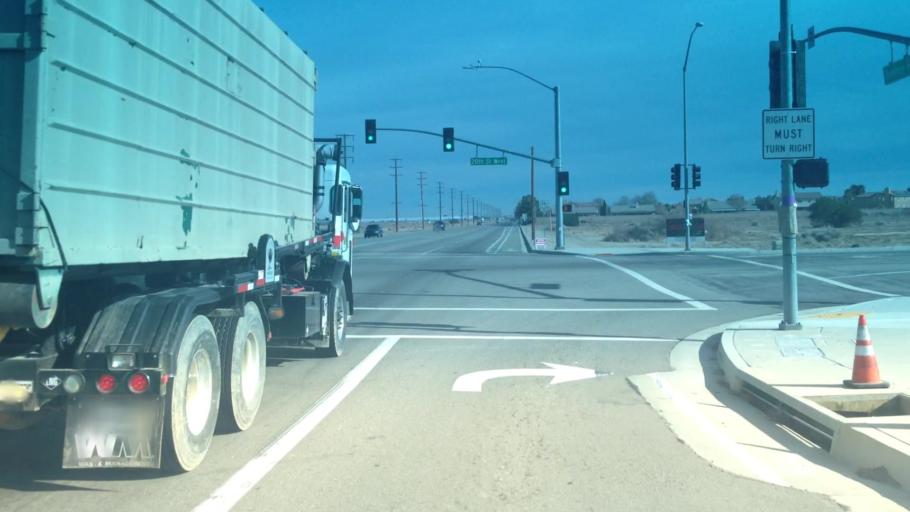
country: US
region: California
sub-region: Los Angeles County
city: Lancaster
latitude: 34.7186
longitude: -118.1666
